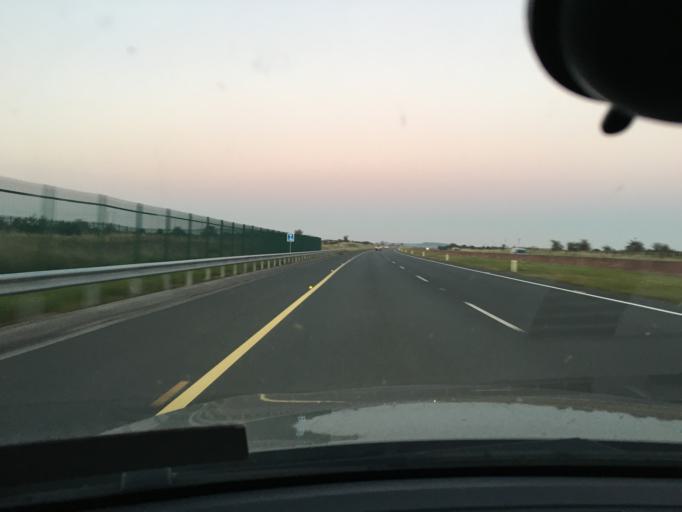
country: IE
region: Connaught
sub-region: County Galway
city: Oranmore
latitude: 53.2980
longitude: -8.8957
